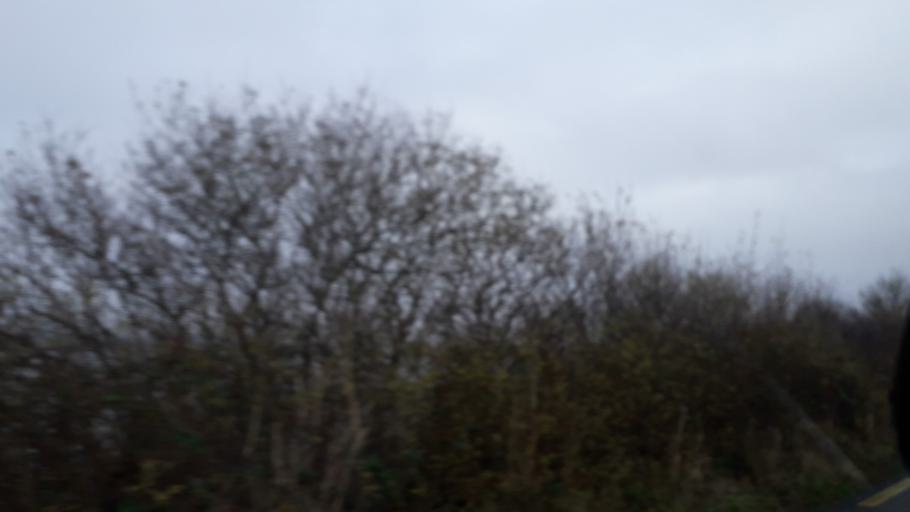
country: IE
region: Ulster
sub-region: County Donegal
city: Buncrana
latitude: 55.1655
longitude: -7.5720
